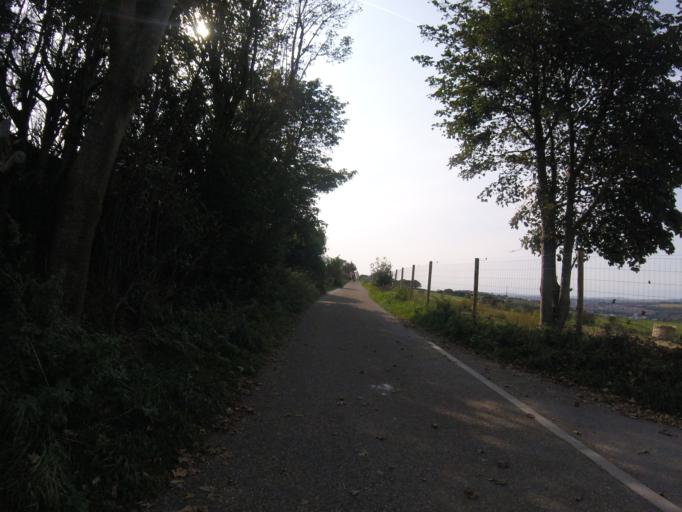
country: GB
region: England
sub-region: Brighton and Hove
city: Rottingdean
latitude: 50.8363
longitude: -0.0890
